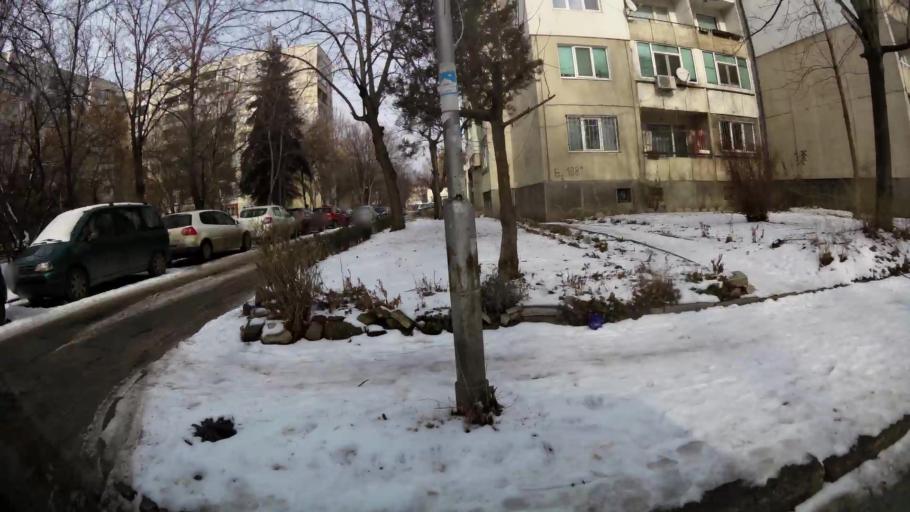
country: BG
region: Sofia-Capital
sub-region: Stolichna Obshtina
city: Sofia
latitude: 42.7052
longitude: 23.3449
